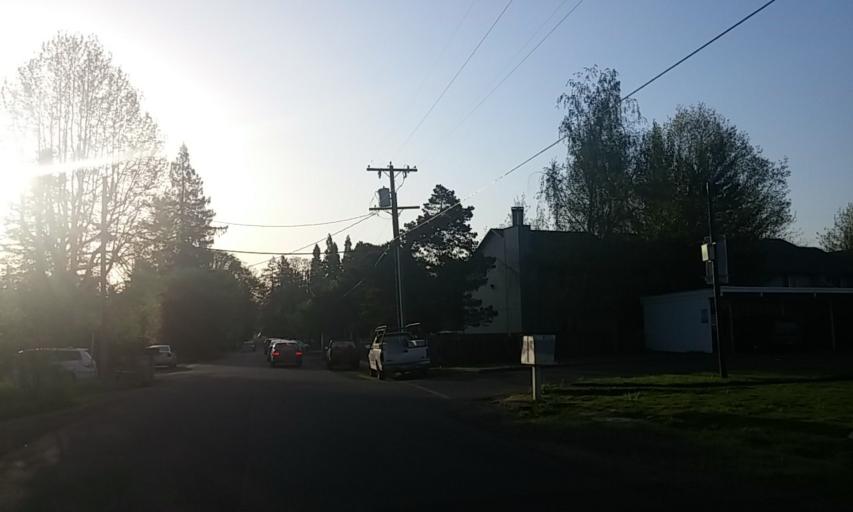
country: US
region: Oregon
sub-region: Washington County
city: Aloha
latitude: 45.4946
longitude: -122.8617
